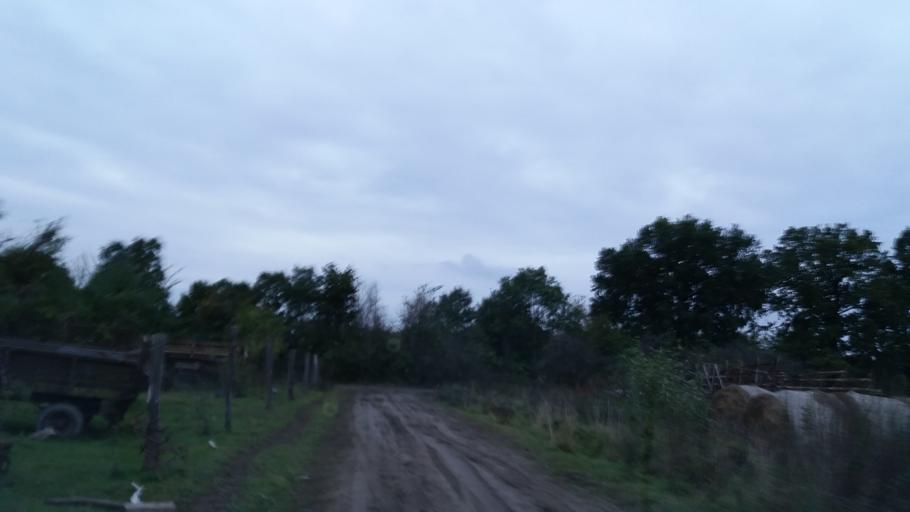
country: PL
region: West Pomeranian Voivodeship
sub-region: Powiat choszczenski
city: Choszczno
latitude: 53.0916
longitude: 15.4003
